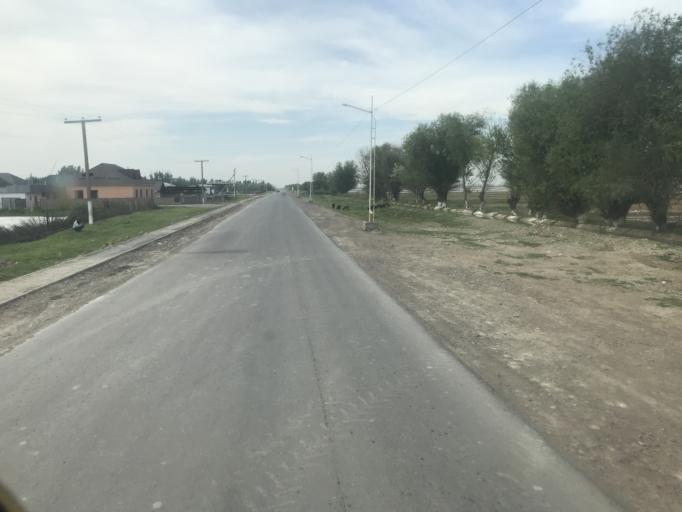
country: KZ
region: Ongtustik Qazaqstan
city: Asykata
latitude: 40.9969
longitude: 68.2119
